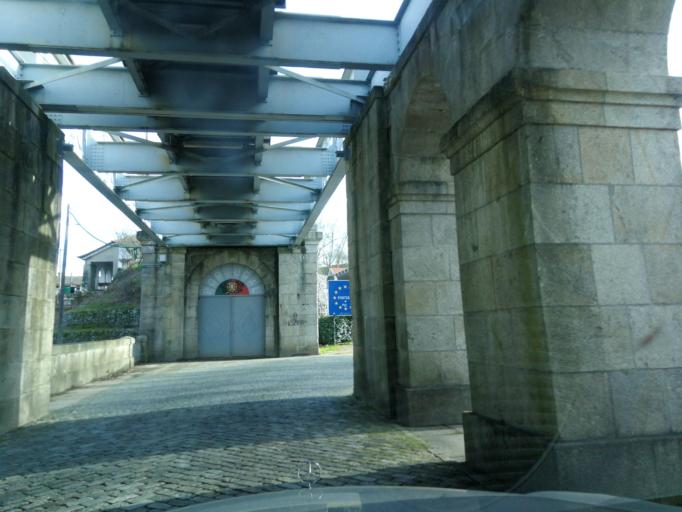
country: PT
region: Viana do Castelo
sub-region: Valenca
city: Valenca
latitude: 42.0355
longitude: -8.6457
